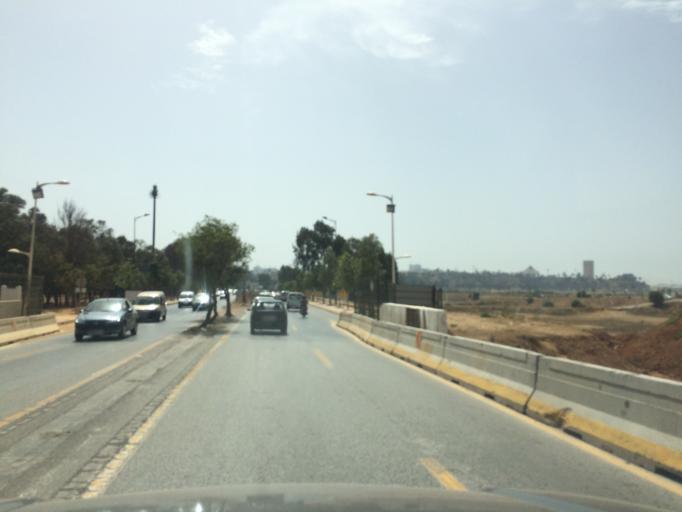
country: MA
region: Rabat-Sale-Zemmour-Zaer
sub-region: Rabat
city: Rabat
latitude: 34.0198
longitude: -6.8074
